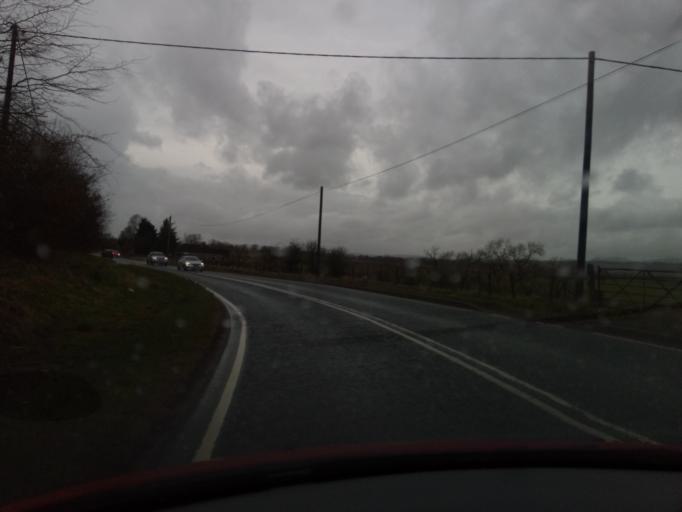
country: GB
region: Scotland
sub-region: East Dunbartonshire
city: Kirkintilloch
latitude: 55.9196
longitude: -4.1795
